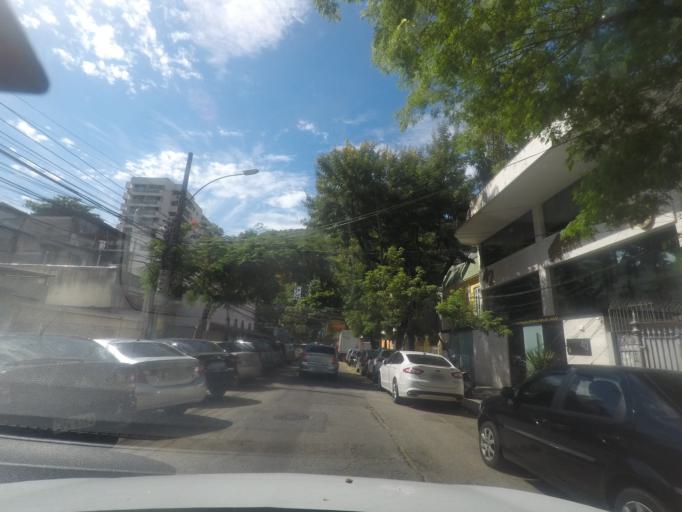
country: BR
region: Rio de Janeiro
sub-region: Rio De Janeiro
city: Rio de Janeiro
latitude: -22.9567
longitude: -43.1963
